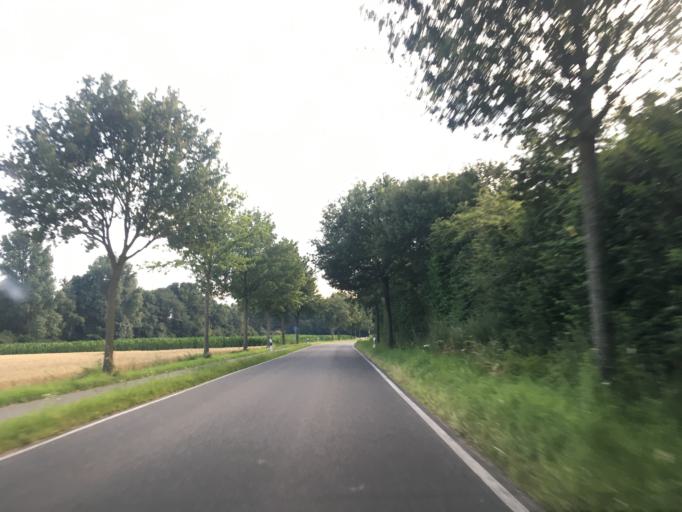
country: DE
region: North Rhine-Westphalia
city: Huckelhoven
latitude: 51.0767
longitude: 6.2086
